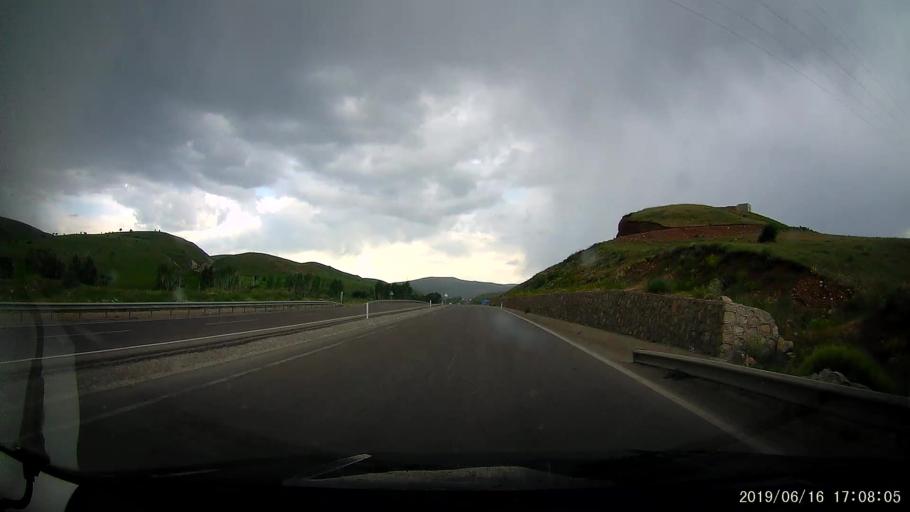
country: TR
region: Erzurum
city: Askale
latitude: 39.9137
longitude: 40.6651
